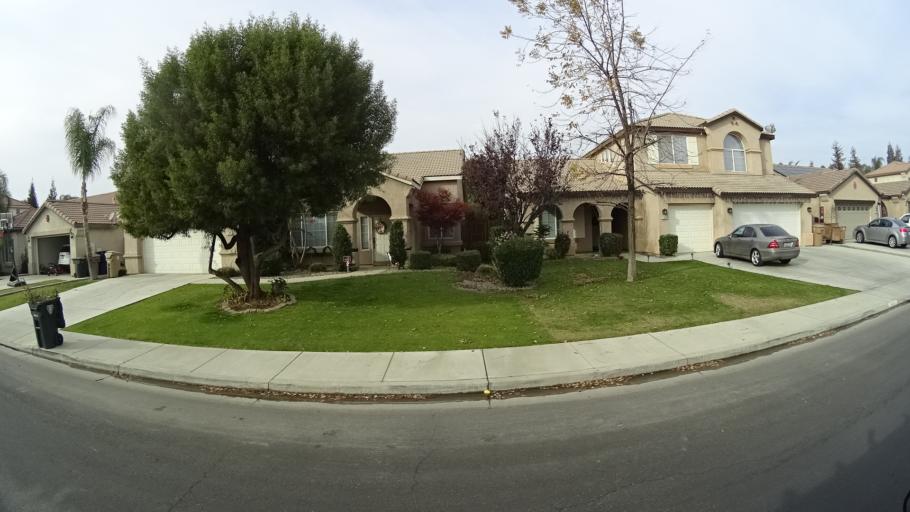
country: US
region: California
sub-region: Kern County
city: Rosedale
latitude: 35.3434
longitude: -119.1351
